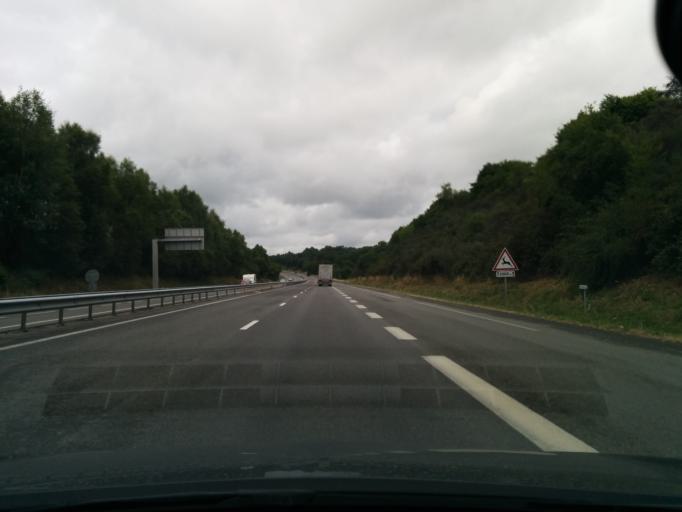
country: FR
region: Limousin
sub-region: Departement de la Haute-Vienne
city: Saint-Germain-les-Belles
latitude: 45.5860
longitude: 1.4712
